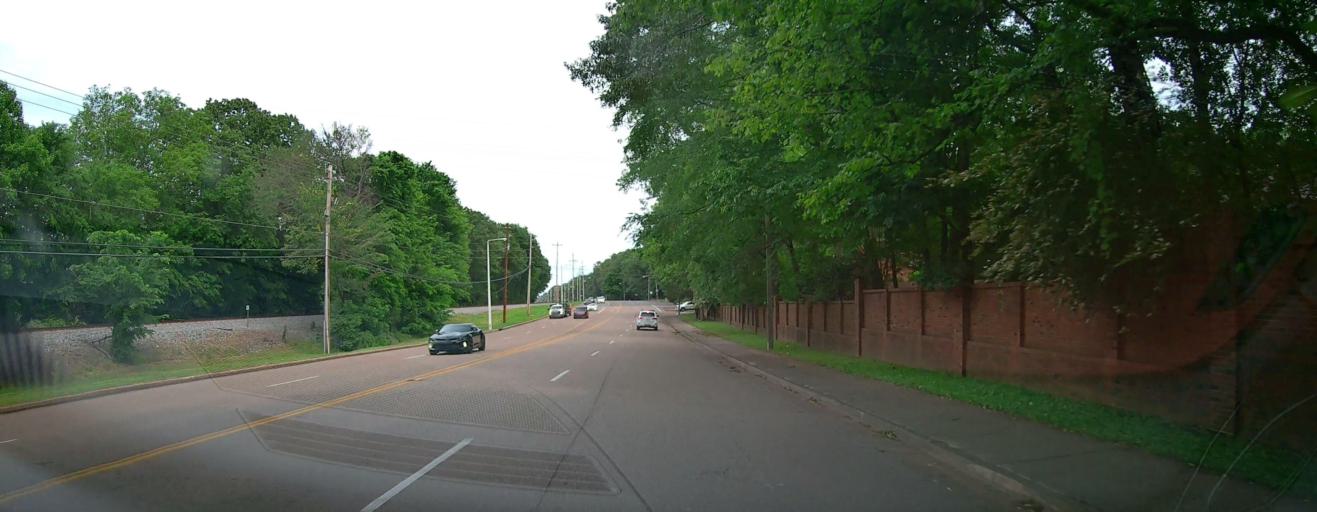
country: US
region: Tennessee
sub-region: Shelby County
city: Germantown
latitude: 35.0972
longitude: -89.8469
